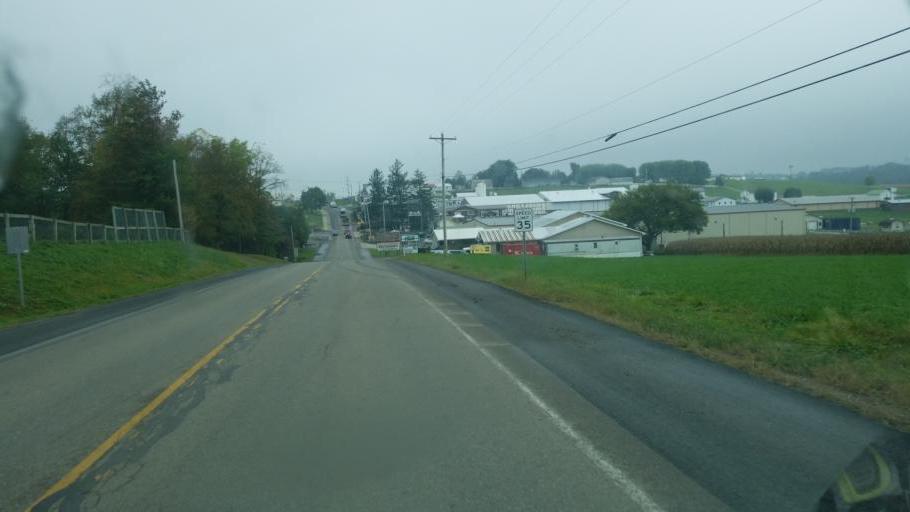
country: US
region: Ohio
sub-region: Holmes County
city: Millersburg
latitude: 40.5765
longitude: -81.7813
